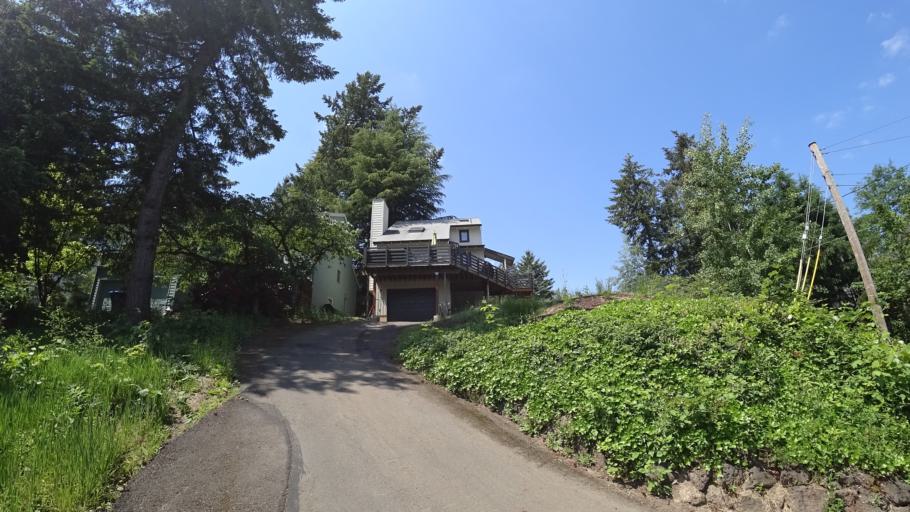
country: US
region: Oregon
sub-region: Washington County
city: Metzger
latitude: 45.4410
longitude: -122.7191
